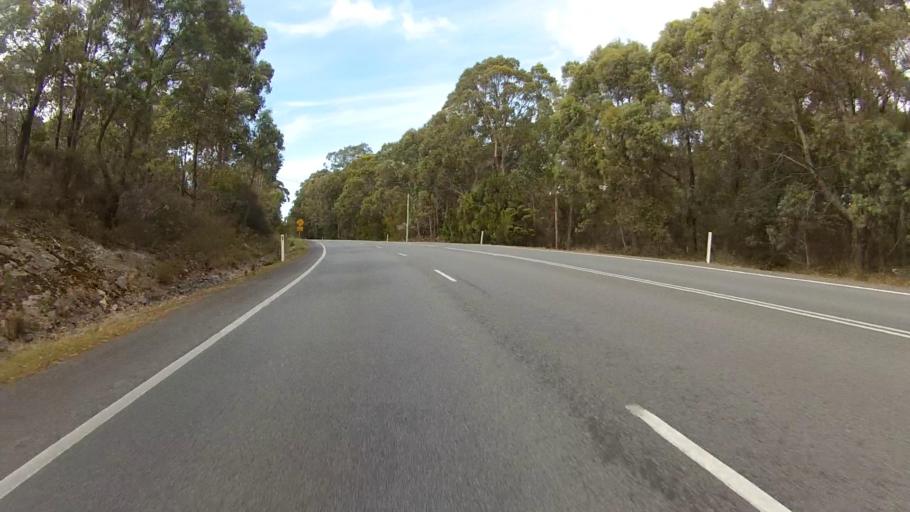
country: AU
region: Tasmania
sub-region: Kingborough
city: Kettering
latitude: -43.1090
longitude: 147.2425
